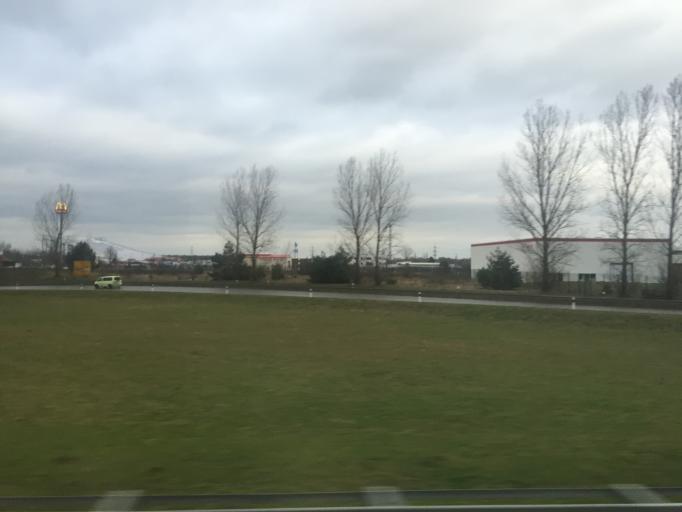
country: DE
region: Mecklenburg-Vorpommern
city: Wittenburg
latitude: 53.4978
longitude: 11.0979
